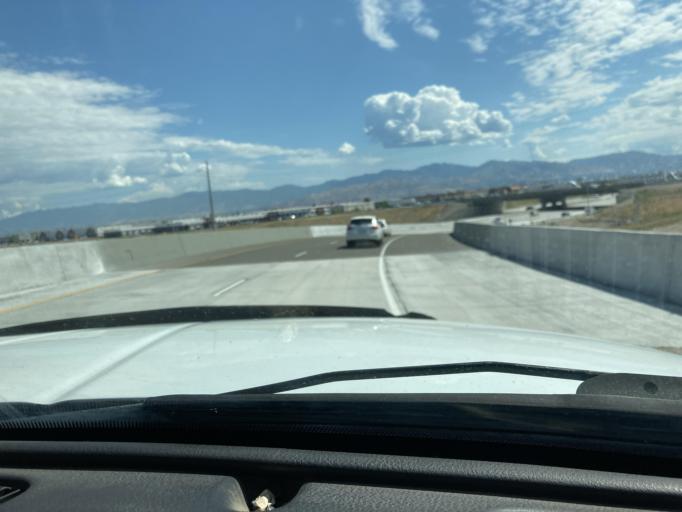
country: US
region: Utah
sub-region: Salt Lake County
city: West Valley City
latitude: 40.7248
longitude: -112.0278
